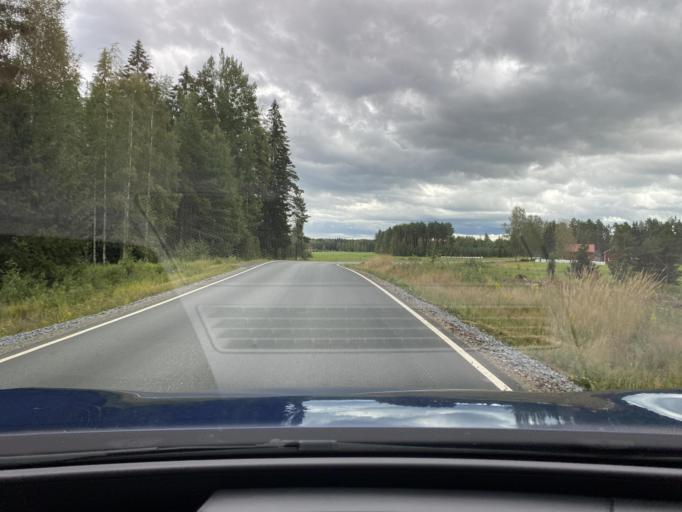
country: FI
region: Pirkanmaa
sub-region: Lounais-Pirkanmaa
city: Vammala
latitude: 61.2829
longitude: 23.0392
